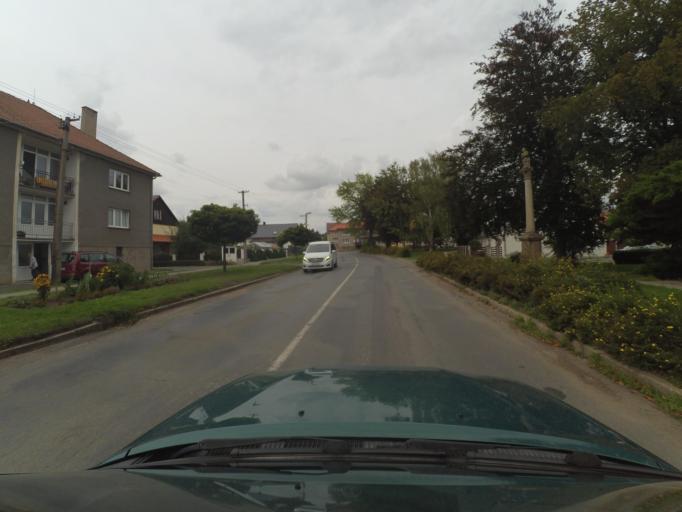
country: CZ
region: Central Bohemia
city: Luzna
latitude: 50.1483
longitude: 13.7419
